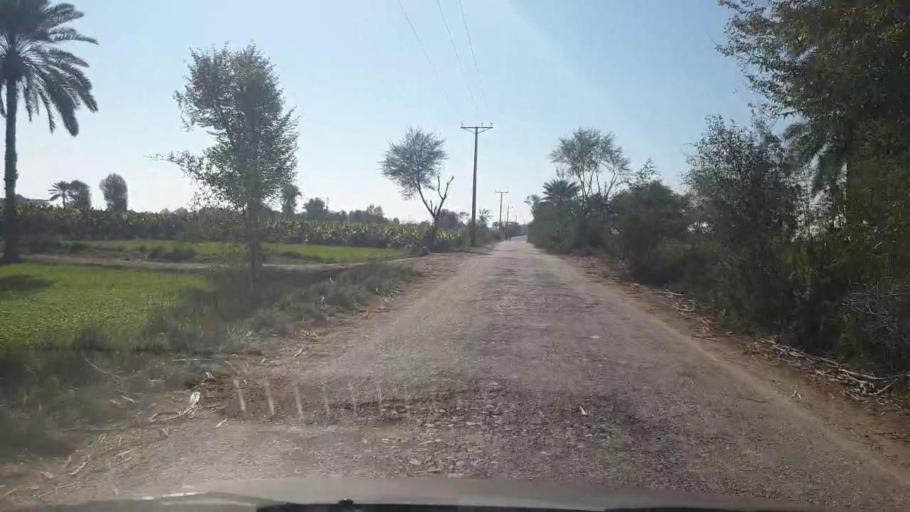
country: PK
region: Sindh
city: Bozdar
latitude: 27.2580
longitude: 68.6526
